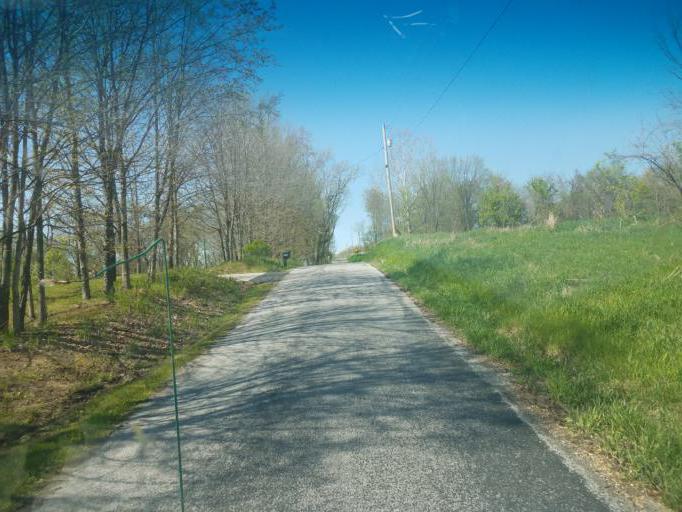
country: US
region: Ohio
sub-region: Medina County
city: Lodi
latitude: 40.9610
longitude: -82.0245
